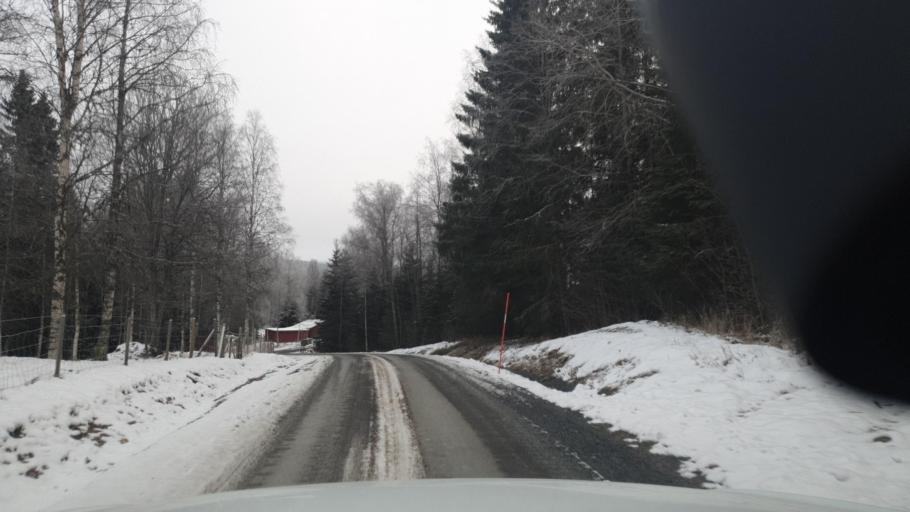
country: SE
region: Vaermland
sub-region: Torsby Kommun
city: Torsby
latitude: 60.1866
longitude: 12.6610
